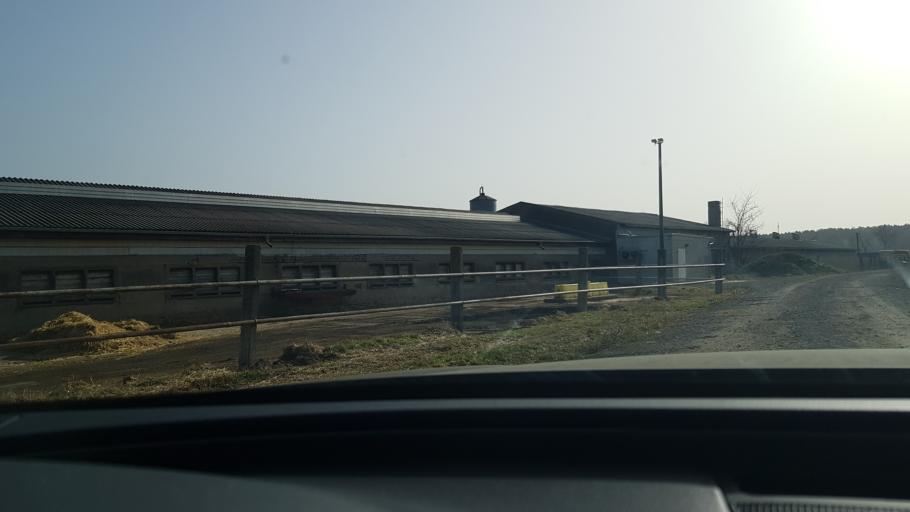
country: DE
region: Brandenburg
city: Schenkendobern
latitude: 51.9586
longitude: 14.6271
